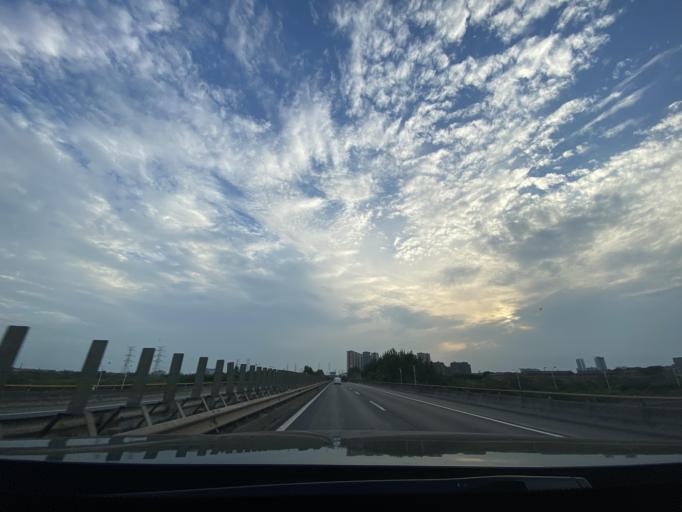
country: CN
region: Sichuan
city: Deyang
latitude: 31.0827
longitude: 104.3956
